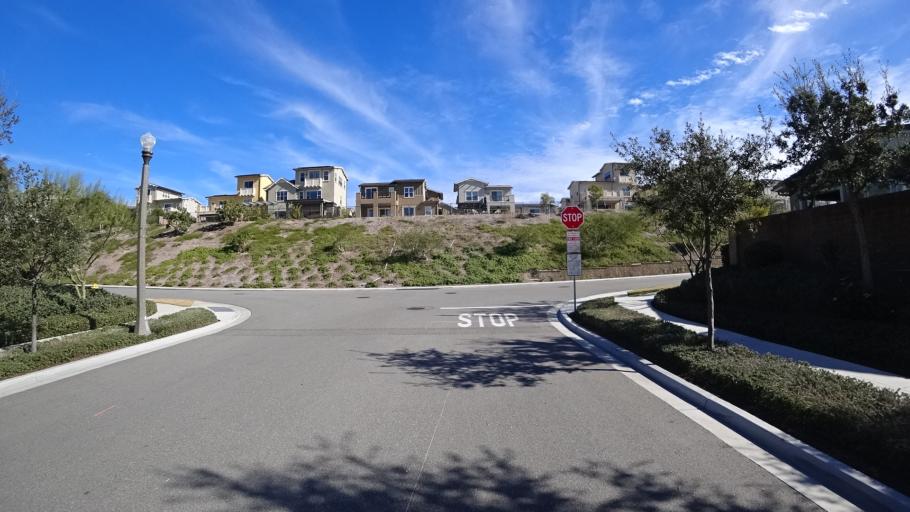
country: US
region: California
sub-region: Orange County
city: Ladera Ranch
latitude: 33.5410
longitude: -117.6007
